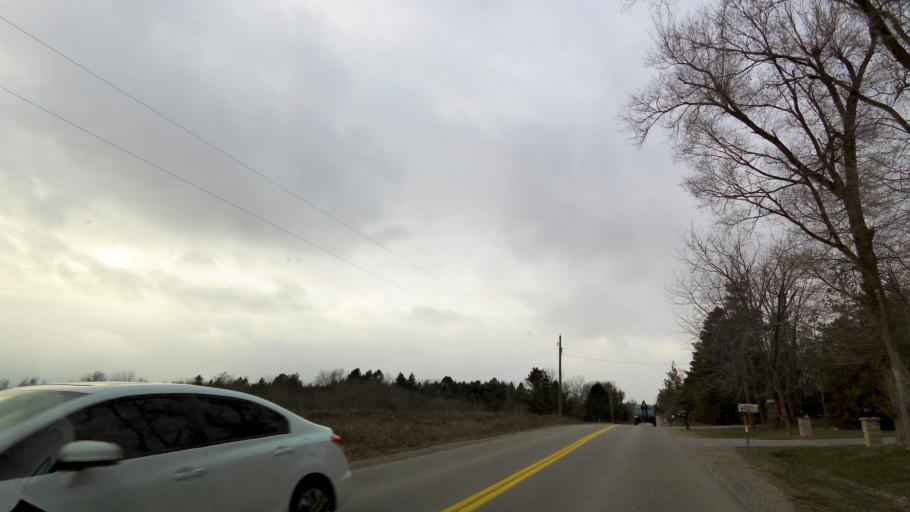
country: CA
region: Ontario
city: Brampton
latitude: 43.8122
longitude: -79.6937
